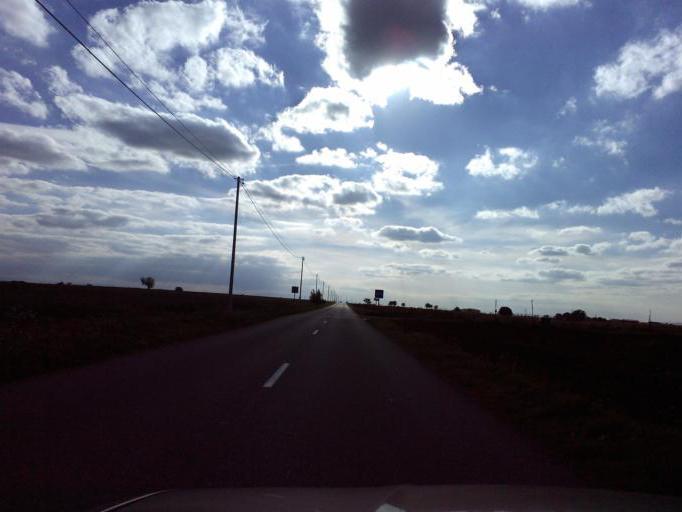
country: FR
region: Provence-Alpes-Cote d'Azur
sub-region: Departement des Alpes-de-Haute-Provence
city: Valensole
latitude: 43.8735
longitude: 6.0221
